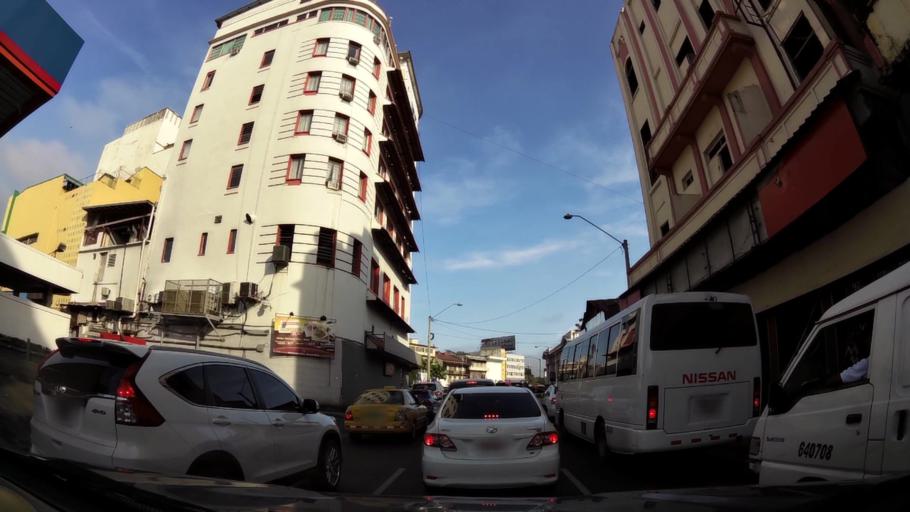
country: PA
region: Panama
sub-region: Distrito de Panama
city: Ancon
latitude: 8.9600
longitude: -79.5405
